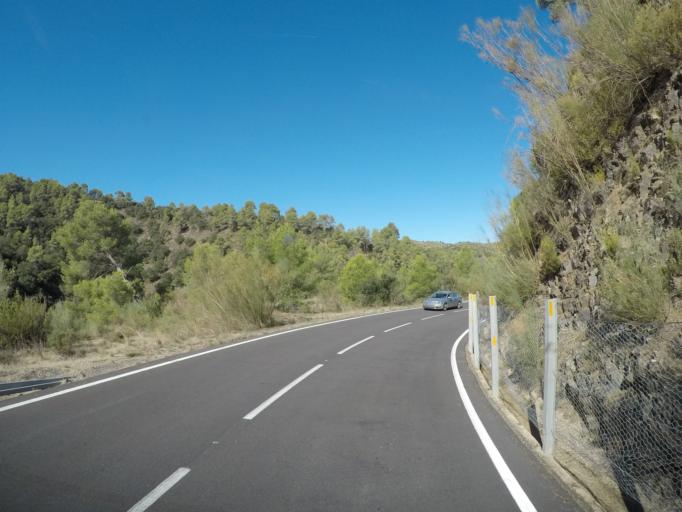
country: ES
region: Catalonia
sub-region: Provincia de Tarragona
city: Falset
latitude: 41.1712
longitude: 0.7987
